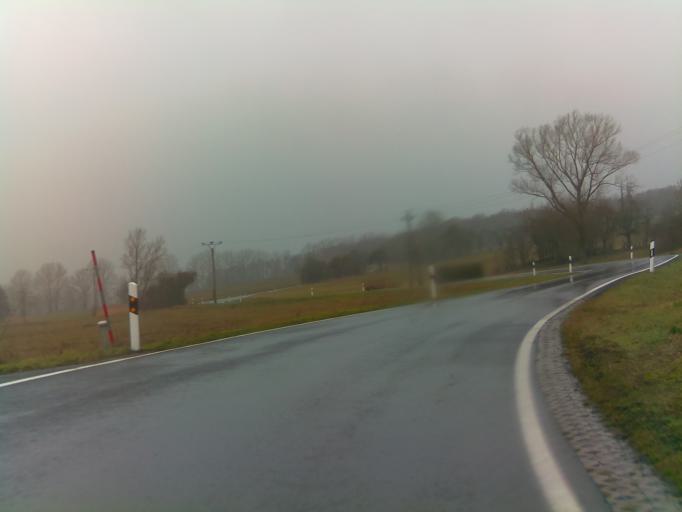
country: DE
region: Thuringia
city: Gleichamberg
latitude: 50.3912
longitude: 10.6434
